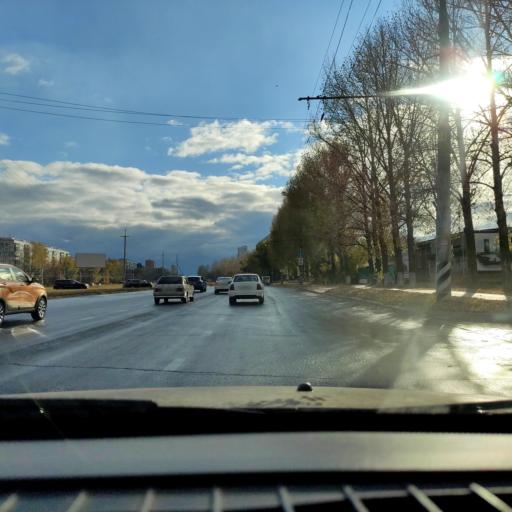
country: RU
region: Samara
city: Tol'yatti
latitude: 53.5239
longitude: 49.2595
